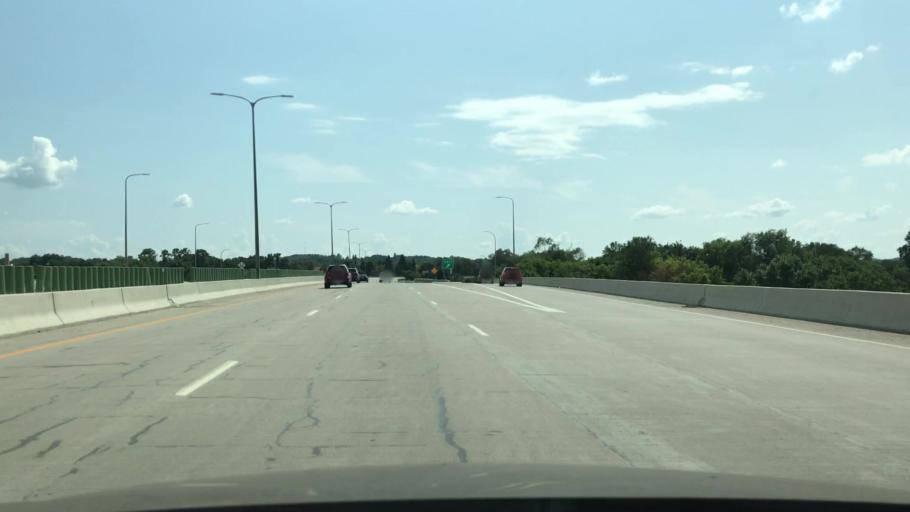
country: US
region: Minnesota
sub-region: Nicollet County
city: North Mankato
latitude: 44.1632
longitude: -94.0182
